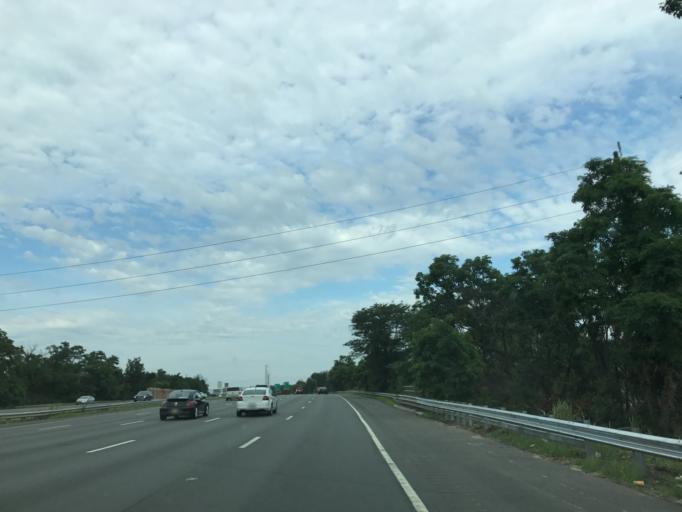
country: US
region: New Jersey
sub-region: Middlesex County
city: Metuchen
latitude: 40.5298
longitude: -74.3445
